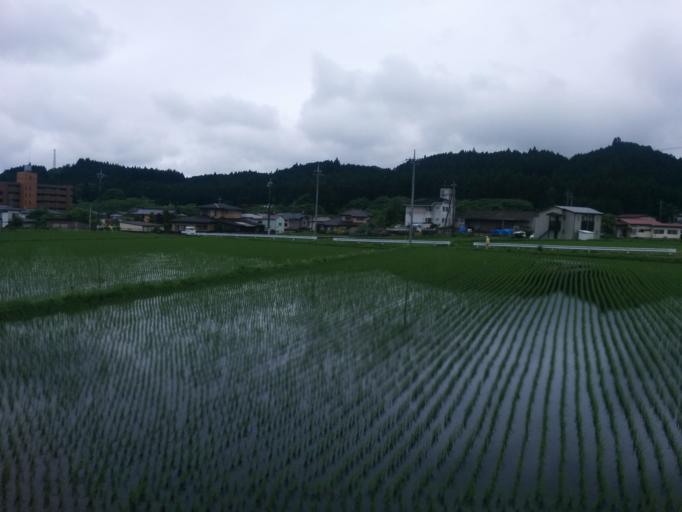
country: JP
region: Tochigi
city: Imaichi
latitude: 36.7249
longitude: 139.6768
